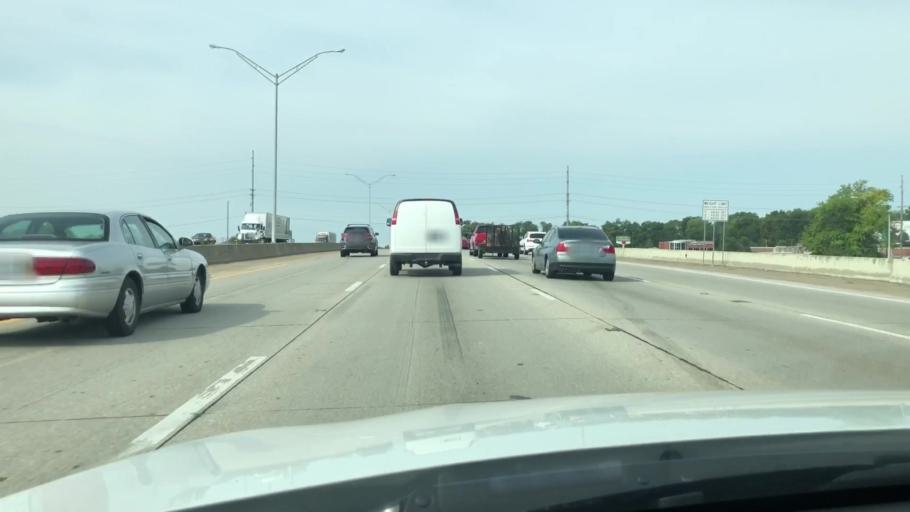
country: US
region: Kentucky
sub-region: Jefferson County
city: West Buechel
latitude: 38.2123
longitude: -85.6697
